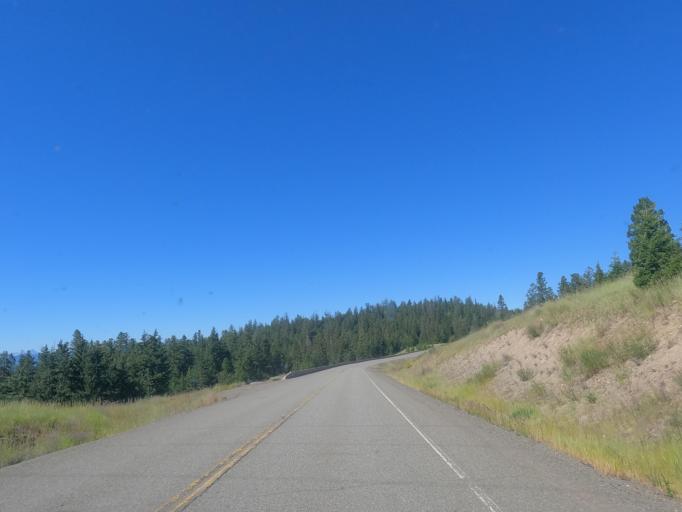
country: CA
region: British Columbia
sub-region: Thompson-Nicola Regional District
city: Ashcroft
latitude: 50.5694
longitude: -121.1889
